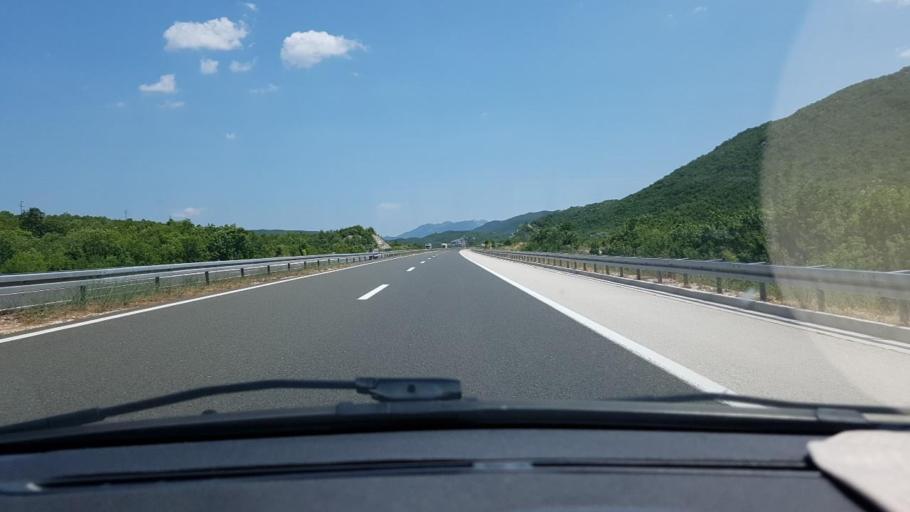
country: HR
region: Splitsko-Dalmatinska
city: Grubine
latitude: 43.3612
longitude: 17.0989
